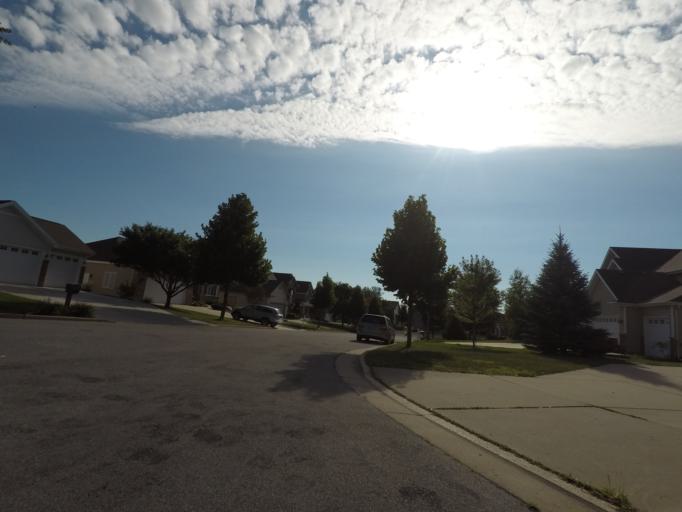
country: US
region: Wisconsin
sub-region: Dane County
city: Middleton
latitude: 43.0716
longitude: -89.5498
